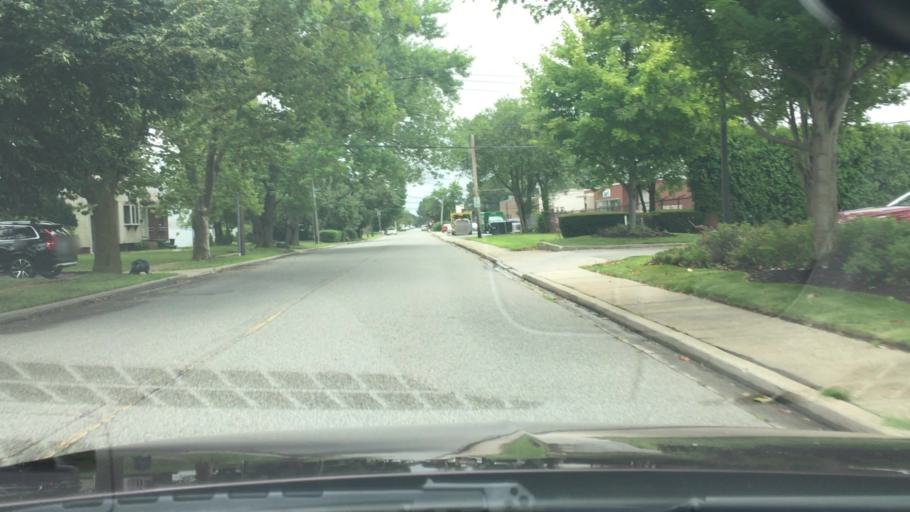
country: US
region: New York
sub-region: Nassau County
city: Hicksville
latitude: 40.7868
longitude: -73.5153
